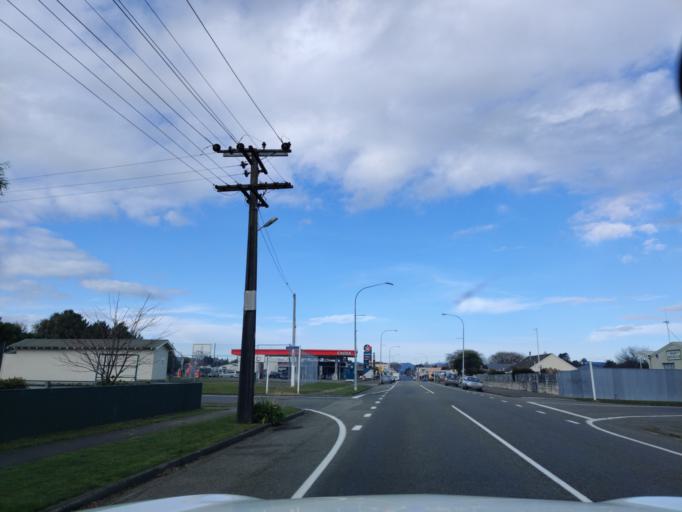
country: NZ
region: Manawatu-Wanganui
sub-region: Palmerston North City
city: Palmerston North
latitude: -40.3363
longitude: 175.8637
